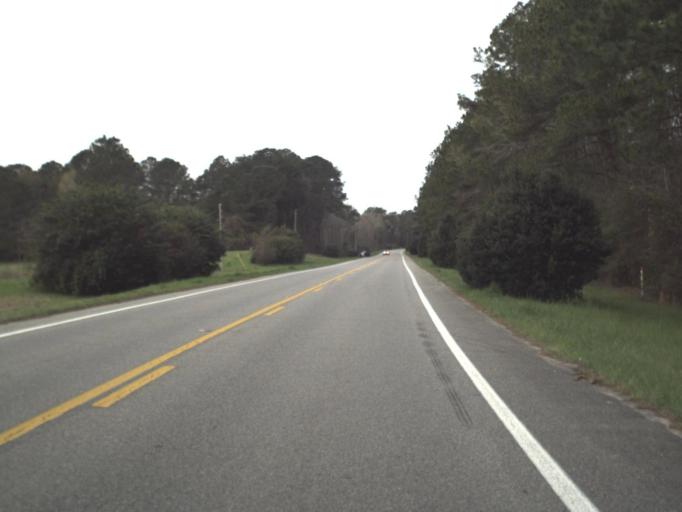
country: US
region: Florida
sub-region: Jefferson County
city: Monticello
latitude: 30.5303
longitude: -83.8197
